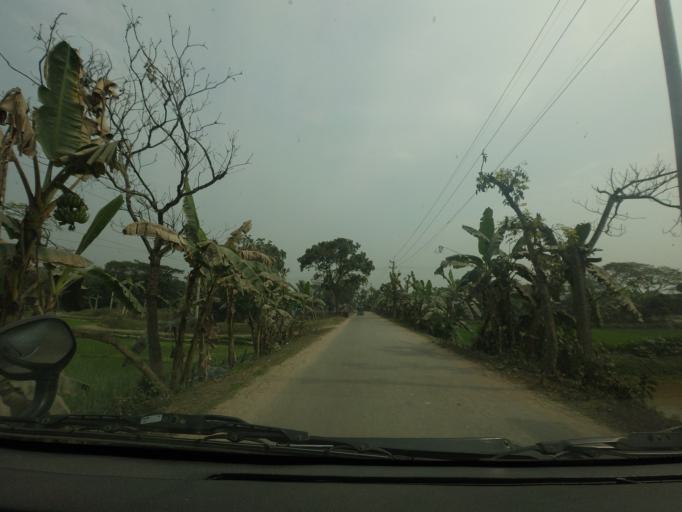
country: BD
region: Dhaka
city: Kishorganj
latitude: 24.3431
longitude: 90.7883
